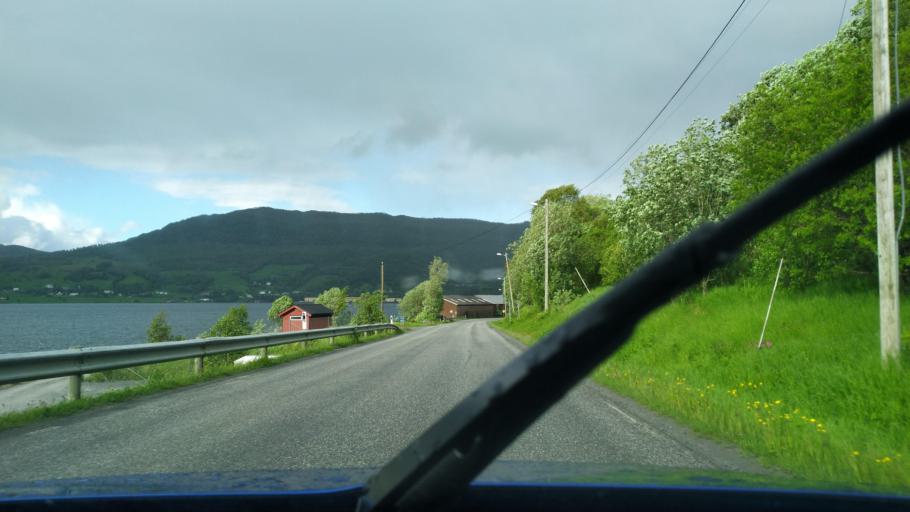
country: NO
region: Troms
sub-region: Sorreisa
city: Sorreisa
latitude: 69.1432
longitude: 18.1273
